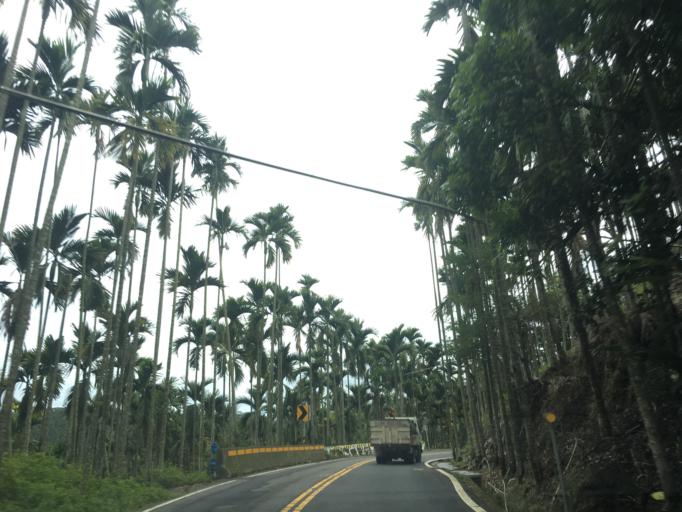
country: TW
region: Taiwan
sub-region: Chiayi
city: Jiayi Shi
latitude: 23.5596
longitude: 120.5801
